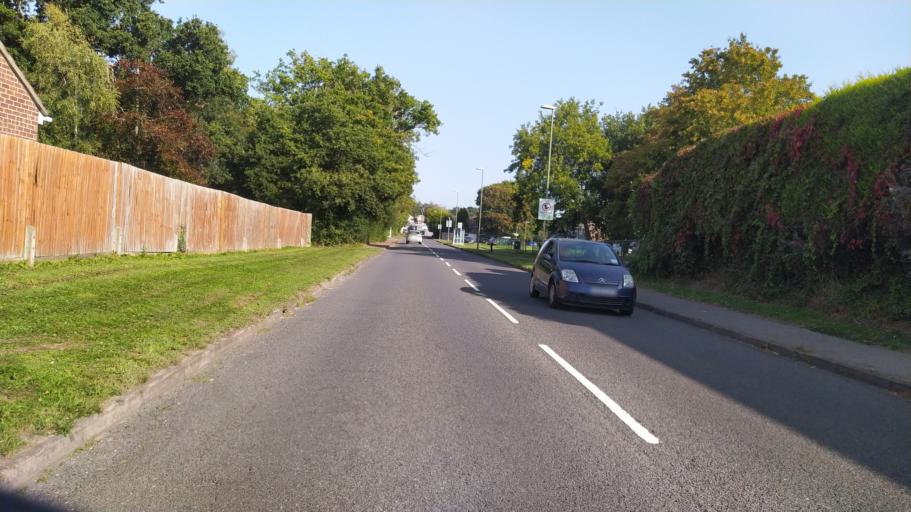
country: GB
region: England
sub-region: Hampshire
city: Hedge End
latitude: 50.9119
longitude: -1.2911
